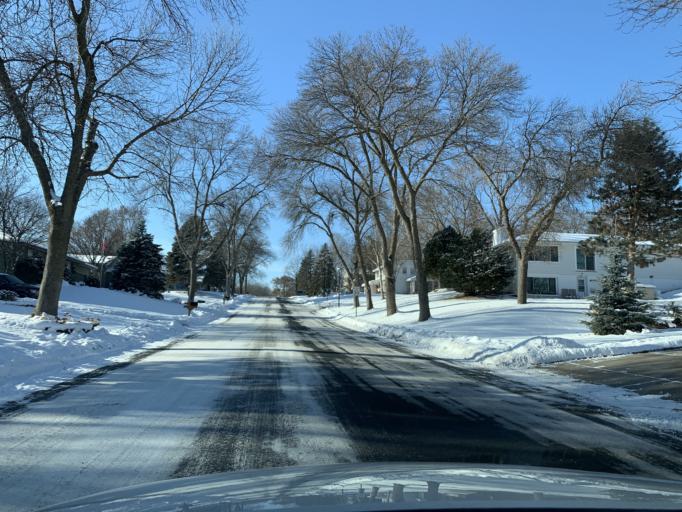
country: US
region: Minnesota
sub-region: Scott County
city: Savage
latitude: 44.8202
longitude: -93.3373
